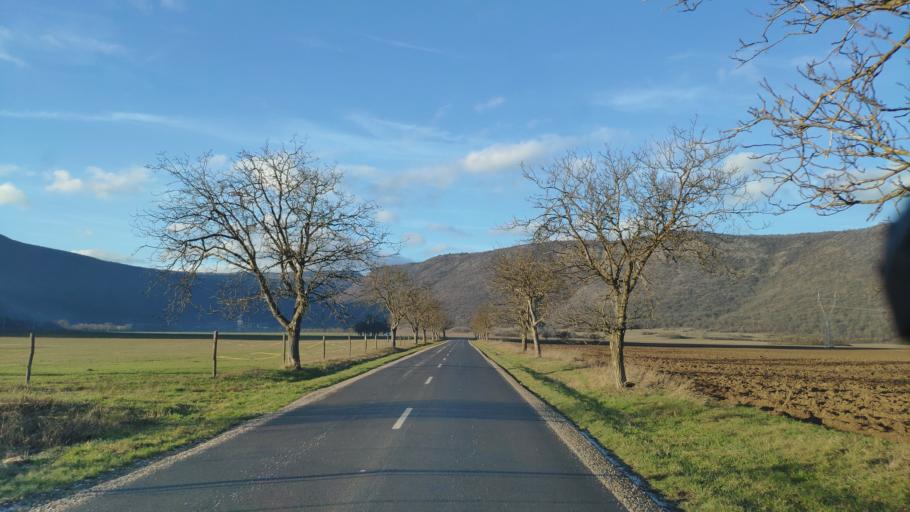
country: SK
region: Kosicky
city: Medzev
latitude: 48.6122
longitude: 20.8838
